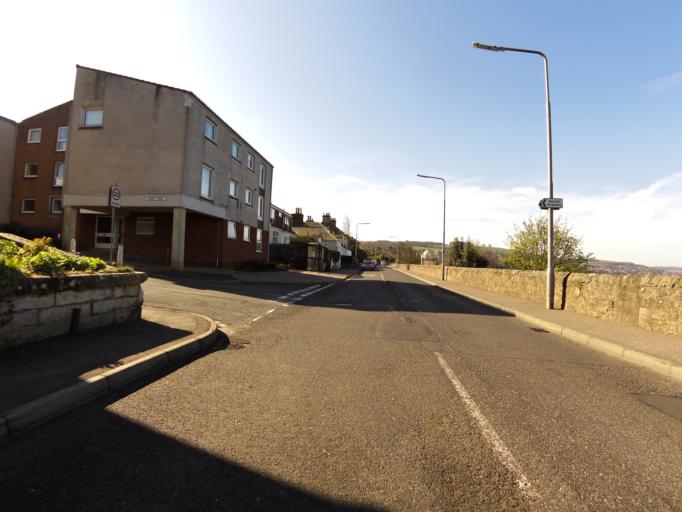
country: GB
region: Scotland
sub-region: Fife
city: Newport-On-Tay
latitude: 56.4423
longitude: -2.9405
